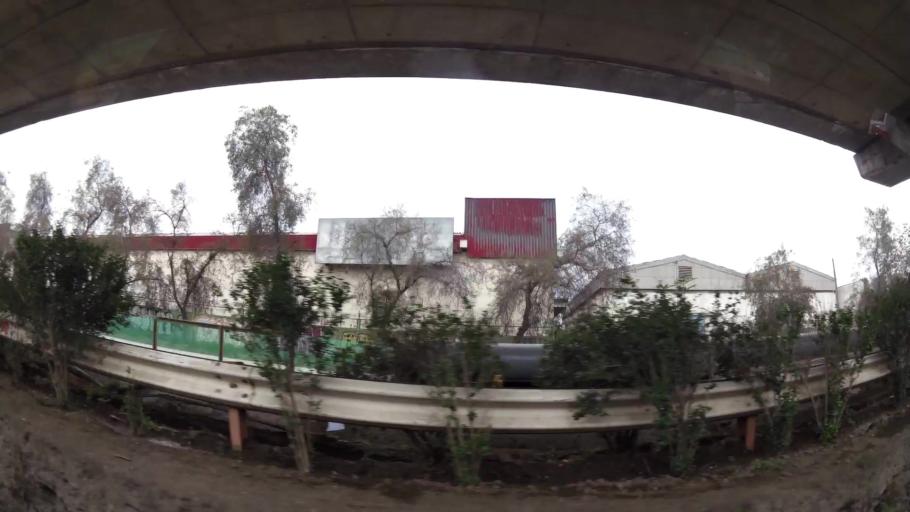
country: CL
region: Santiago Metropolitan
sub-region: Provincia de Santiago
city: Santiago
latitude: -33.4745
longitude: -70.6232
